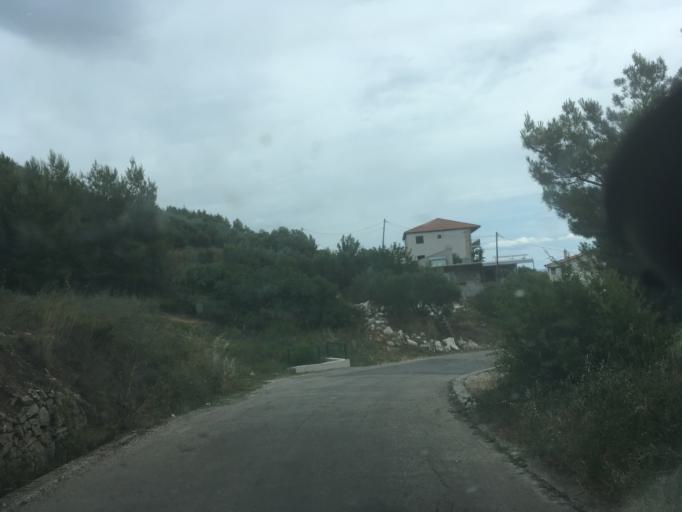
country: HR
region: Splitsko-Dalmatinska
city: Jesenice
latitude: 43.4576
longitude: 16.6203
